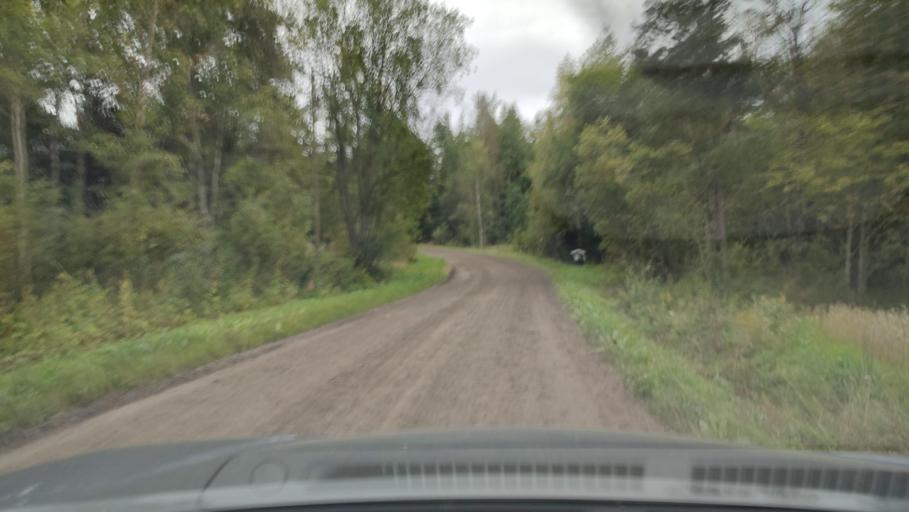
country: FI
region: Southern Ostrobothnia
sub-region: Suupohja
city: Karijoki
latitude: 62.2346
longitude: 21.5707
